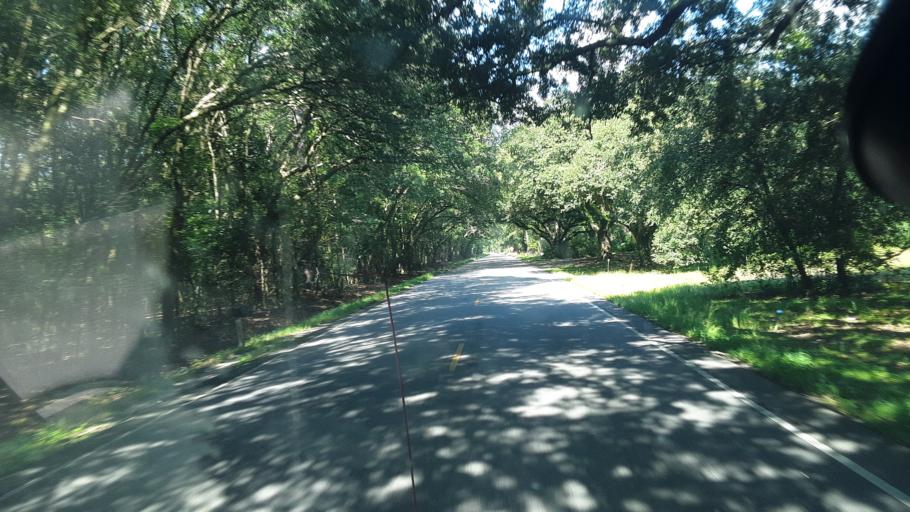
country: US
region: South Carolina
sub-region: Jasper County
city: Ridgeland
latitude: 32.5910
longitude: -80.9713
